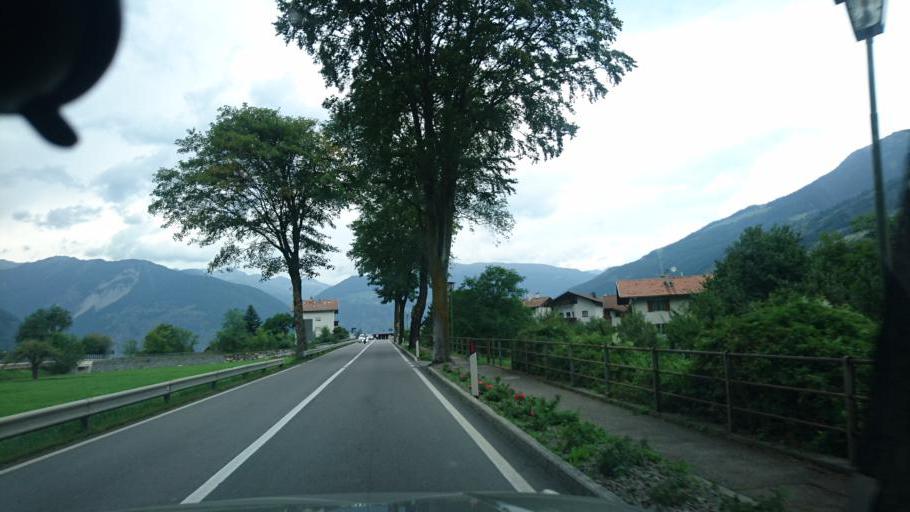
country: IT
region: Trentino-Alto Adige
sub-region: Bolzano
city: Sluderno
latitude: 46.6618
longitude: 10.5854
